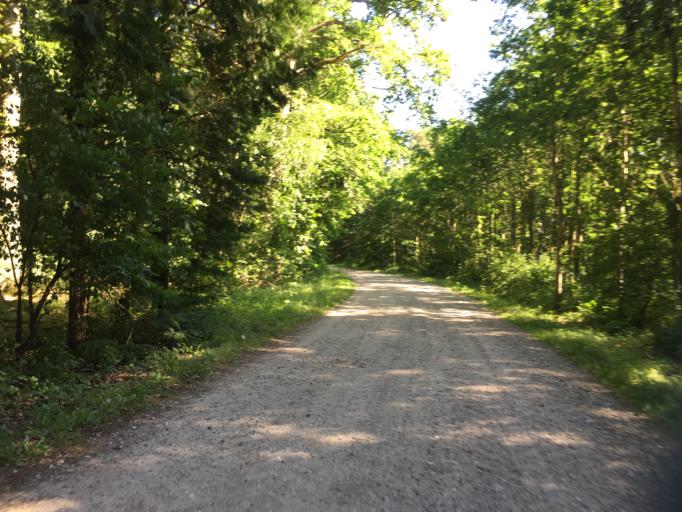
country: DK
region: South Denmark
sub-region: Kerteminde Kommune
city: Langeskov
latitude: 55.3638
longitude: 10.5499
